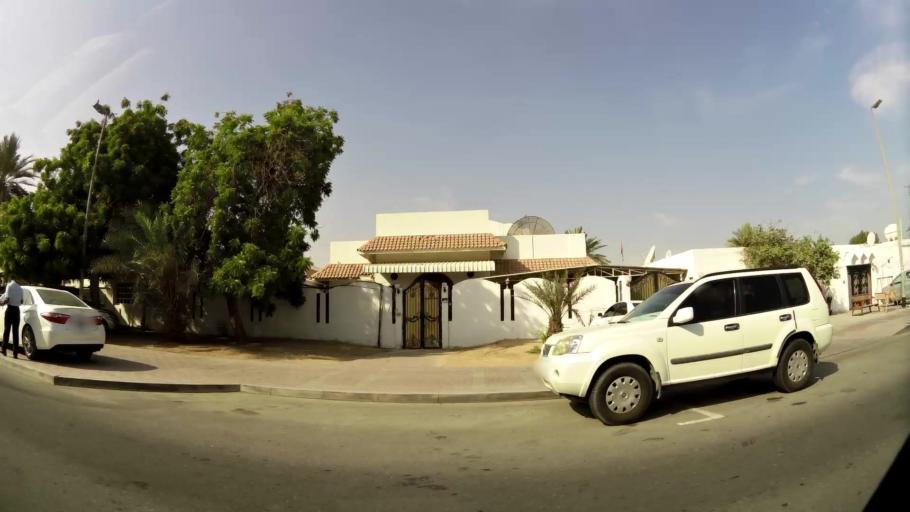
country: AE
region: Ash Shariqah
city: Sharjah
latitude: 25.2189
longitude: 55.3885
